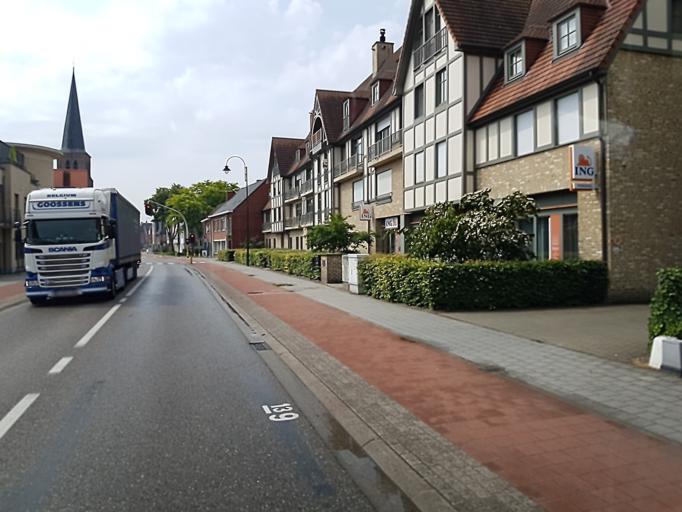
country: BE
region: Flanders
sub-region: Provincie Antwerpen
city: Dessel
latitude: 51.2415
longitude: 5.1126
